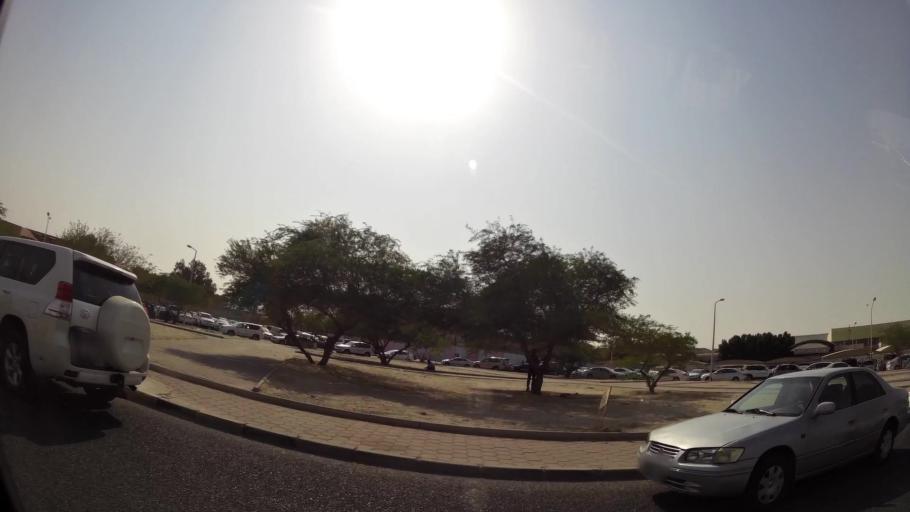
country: KW
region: Muhafazat al Jahra'
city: Al Jahra'
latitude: 29.3427
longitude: 47.6555
